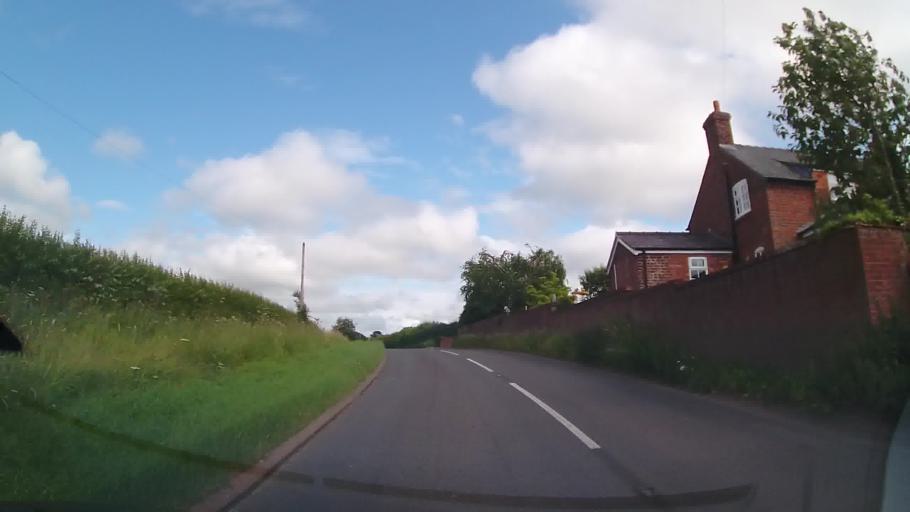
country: GB
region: England
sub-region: Shropshire
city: Pant
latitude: 52.8008
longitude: -3.0163
